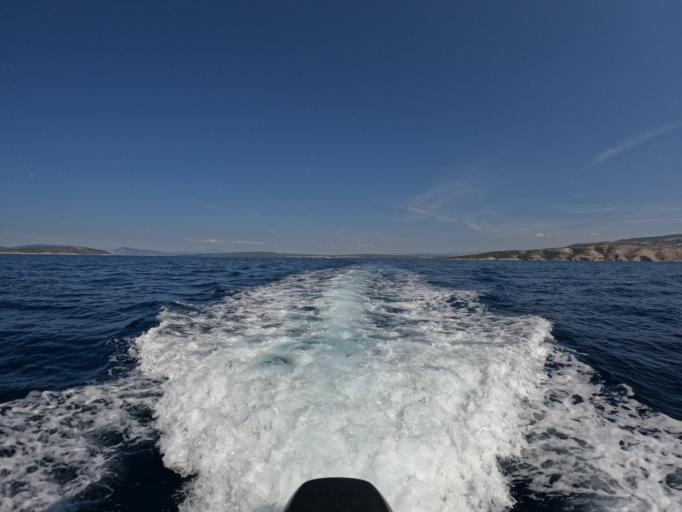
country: HR
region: Primorsko-Goranska
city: Punat
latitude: 44.9477
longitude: 14.6132
